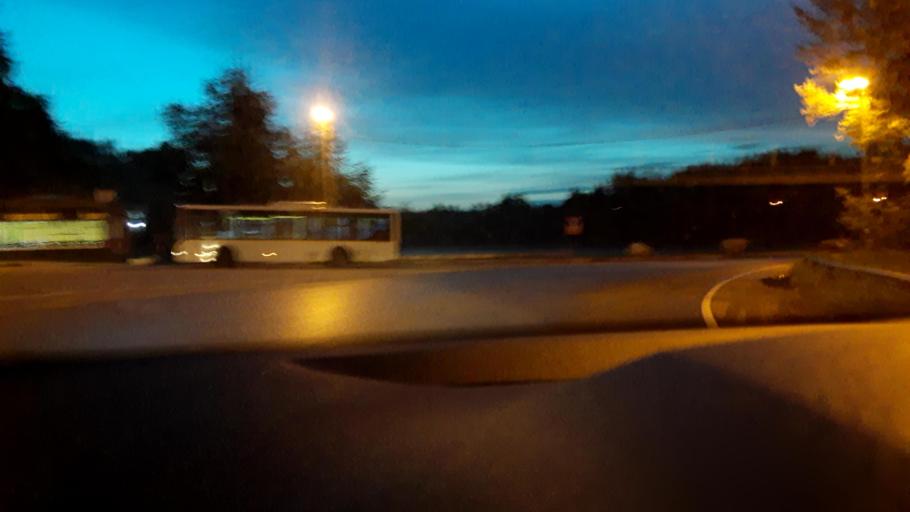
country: RU
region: Moskovskaya
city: Petrovo-Dal'neye
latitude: 55.7964
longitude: 37.1994
